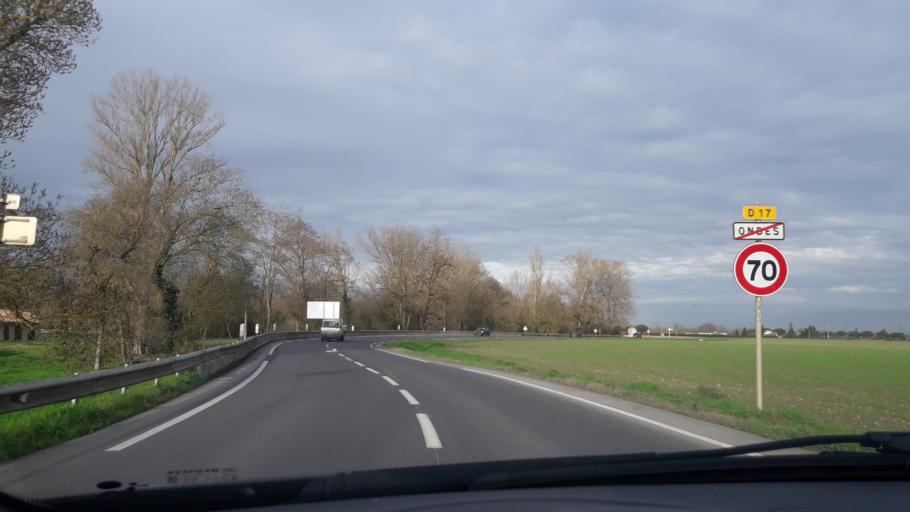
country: FR
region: Midi-Pyrenees
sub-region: Departement de la Haute-Garonne
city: Ondes
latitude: 43.7808
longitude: 1.3066
